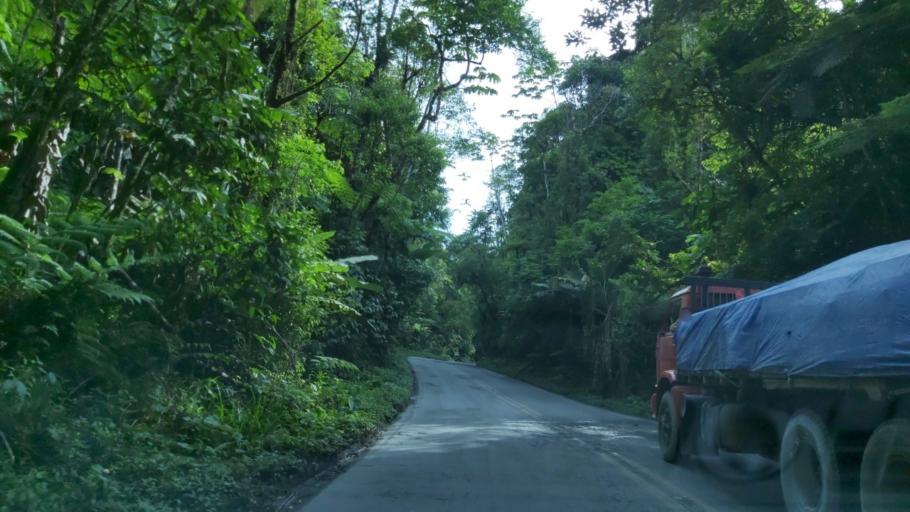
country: BR
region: Sao Paulo
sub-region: Miracatu
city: Miracatu
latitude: -24.0336
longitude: -47.5609
